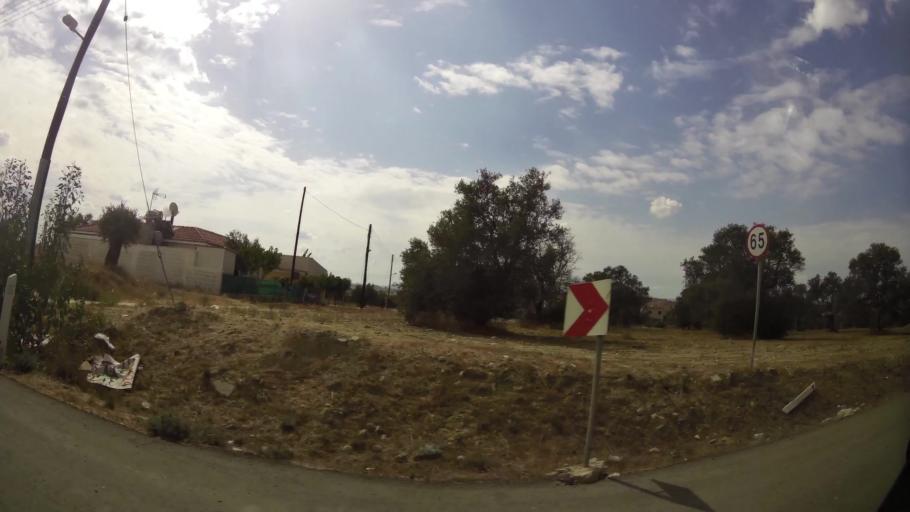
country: CY
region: Lefkosia
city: Tseri
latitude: 35.0670
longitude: 33.3341
